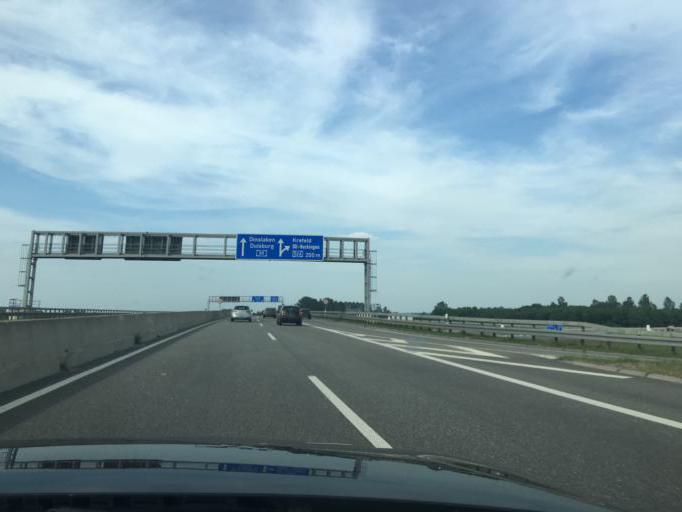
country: DE
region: North Rhine-Westphalia
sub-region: Regierungsbezirk Dusseldorf
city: Hochfeld
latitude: 51.3519
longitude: 6.7572
